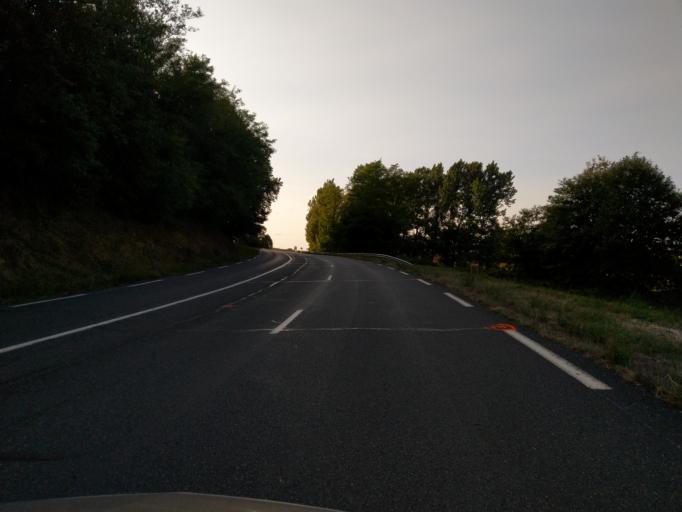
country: FR
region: Midi-Pyrenees
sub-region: Departement du Tarn
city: Realmont
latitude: 43.8006
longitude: 2.1858
